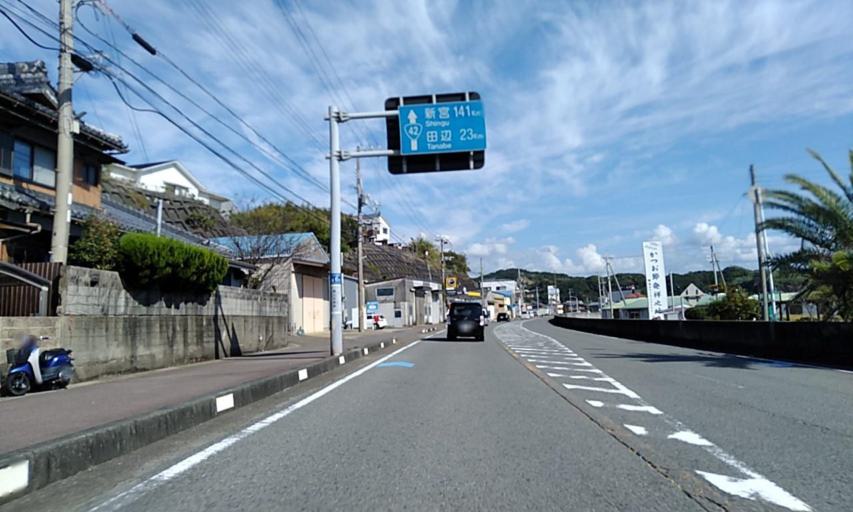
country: JP
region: Wakayama
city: Gobo
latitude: 33.8143
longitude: 135.2138
